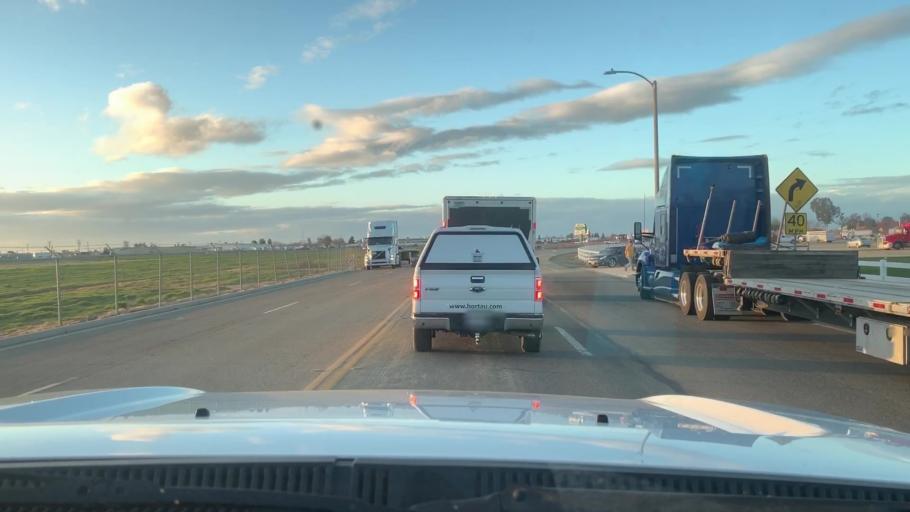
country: US
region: California
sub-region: Tulare County
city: Tulare
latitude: 36.1603
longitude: -119.3284
